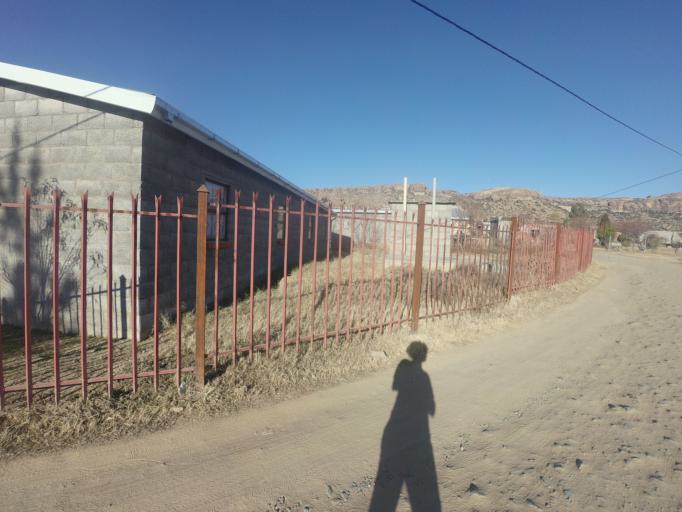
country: LS
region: Maseru
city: Maseru
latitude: -29.2989
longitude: 27.5458
